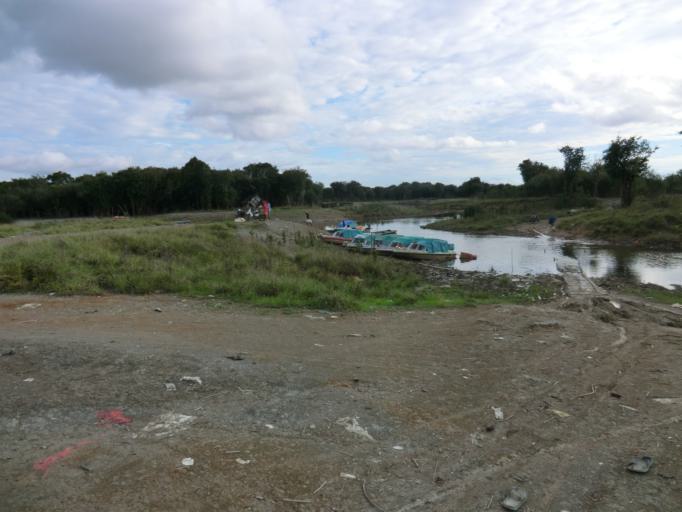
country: MY
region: Sarawak
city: Simanggang
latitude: 1.0151
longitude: 112.2177
